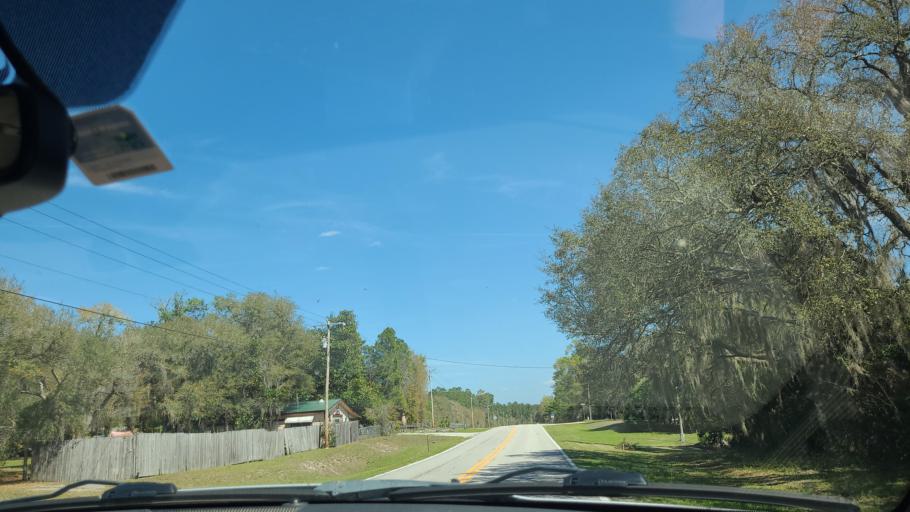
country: US
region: Florida
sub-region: Putnam County
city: Crescent City
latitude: 29.3782
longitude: -81.7631
